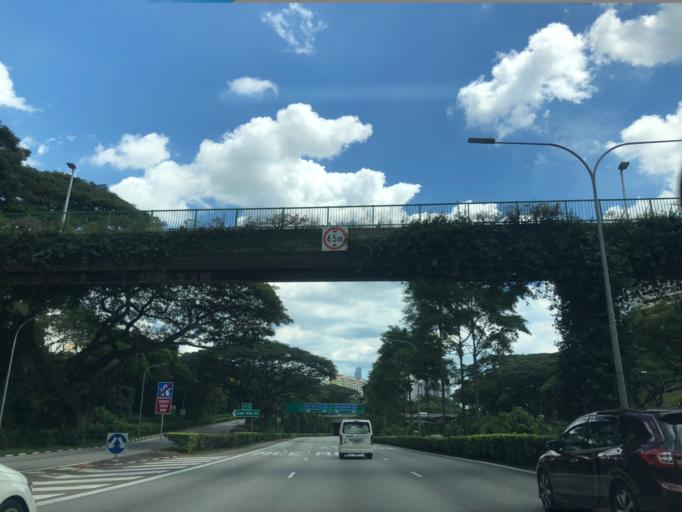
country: SG
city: Singapore
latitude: 1.2790
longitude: 103.8210
